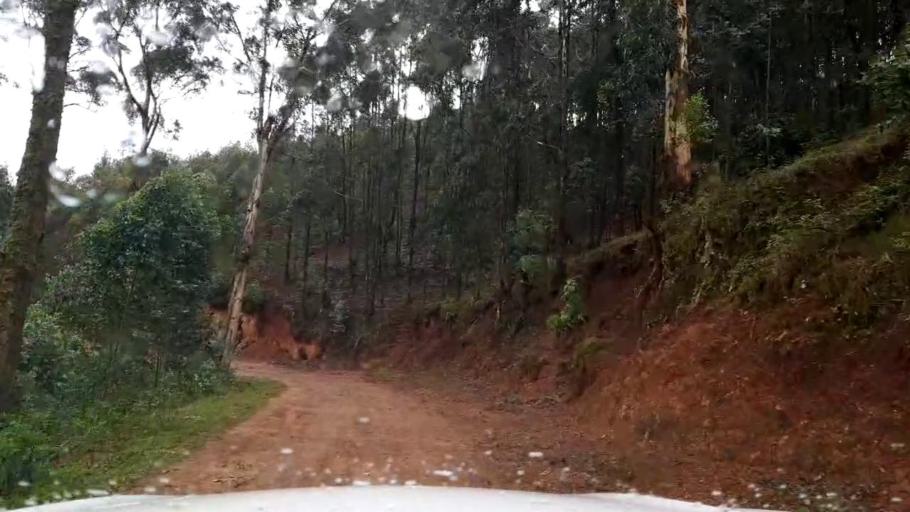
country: RW
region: Western Province
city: Kibuye
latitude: -2.0265
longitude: 29.4519
